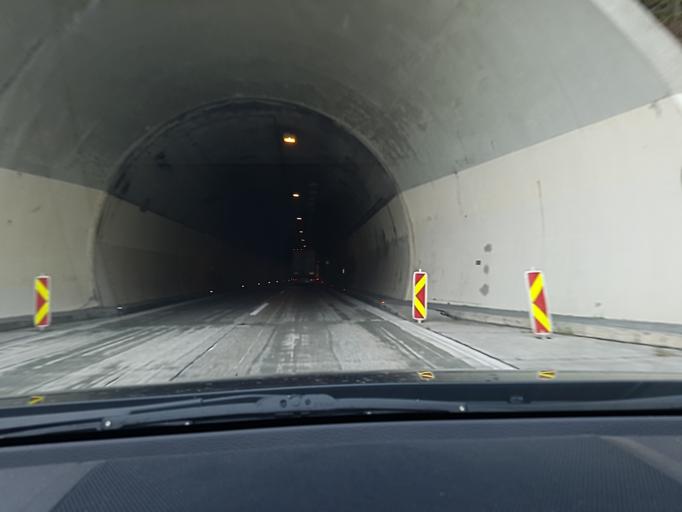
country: AT
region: Salzburg
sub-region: Politischer Bezirk Sankt Johann im Pongau
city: Werfen
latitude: 47.4889
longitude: 13.1872
